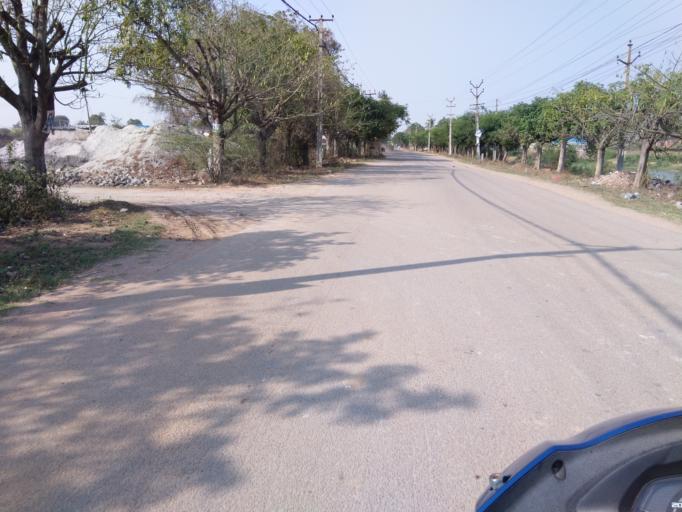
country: IN
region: Telangana
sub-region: Rangareddi
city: Quthbullapur
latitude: 17.5848
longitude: 78.4193
